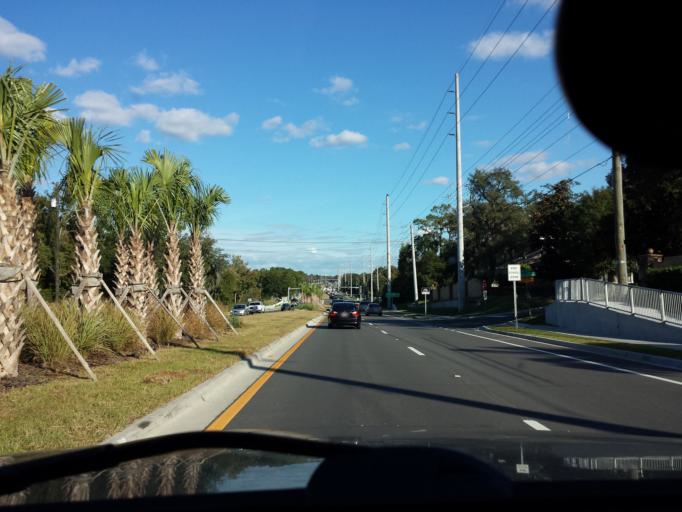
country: US
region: Florida
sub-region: Hillsborough County
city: Riverview
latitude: 27.8535
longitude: -82.2816
